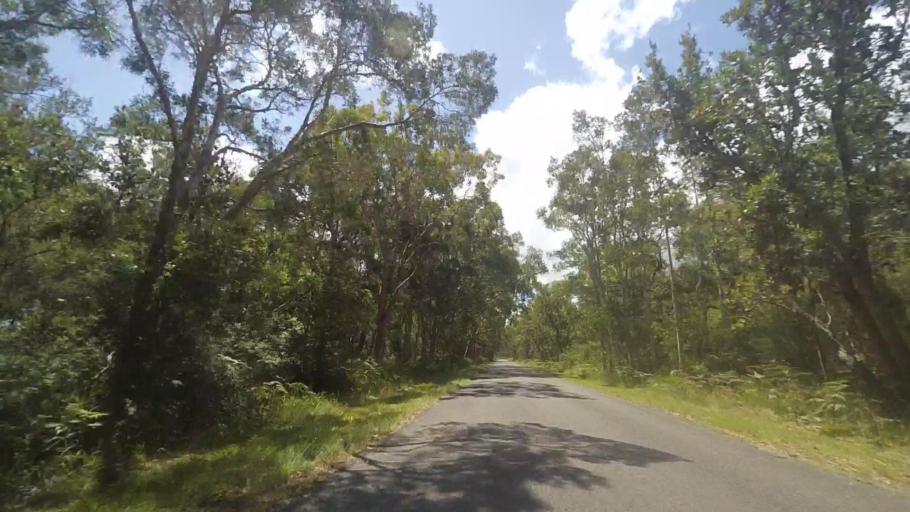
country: AU
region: New South Wales
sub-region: Great Lakes
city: Bulahdelah
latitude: -32.5136
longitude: 152.3215
